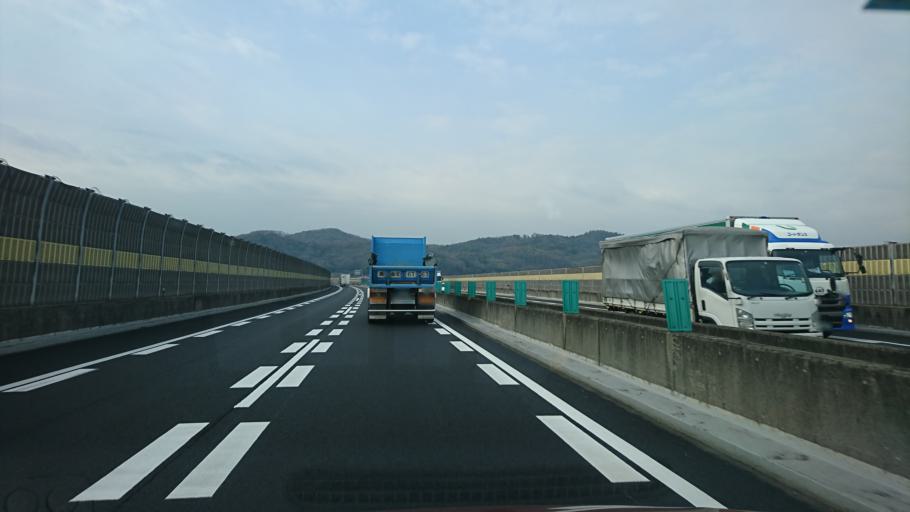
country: JP
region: Okayama
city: Okayama-shi
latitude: 34.6923
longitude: 133.8676
